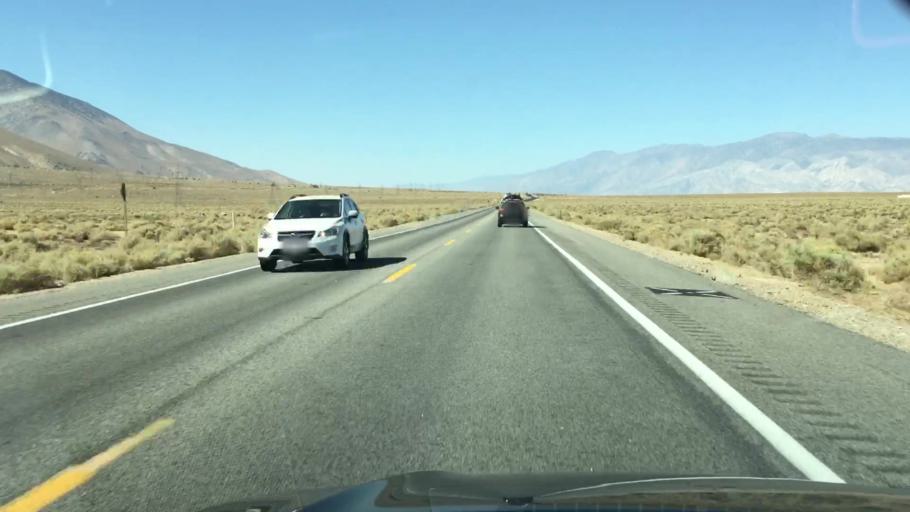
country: US
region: California
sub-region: Inyo County
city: Lone Pine
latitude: 36.3678
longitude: -118.0238
